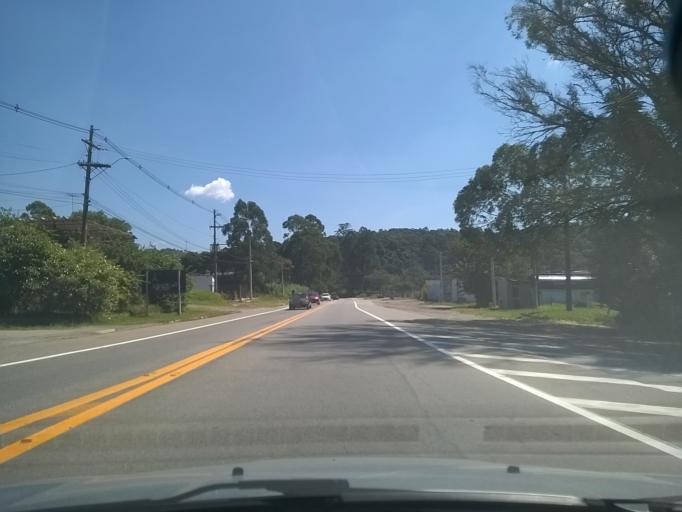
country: BR
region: Sao Paulo
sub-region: Varzea Paulista
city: Varzea Paulista
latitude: -23.2509
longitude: -46.8382
